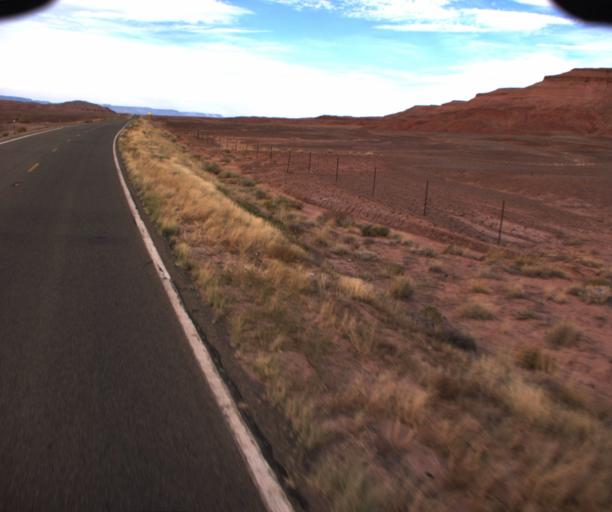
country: US
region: Arizona
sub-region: Apache County
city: Many Farms
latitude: 36.4698
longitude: -109.5259
